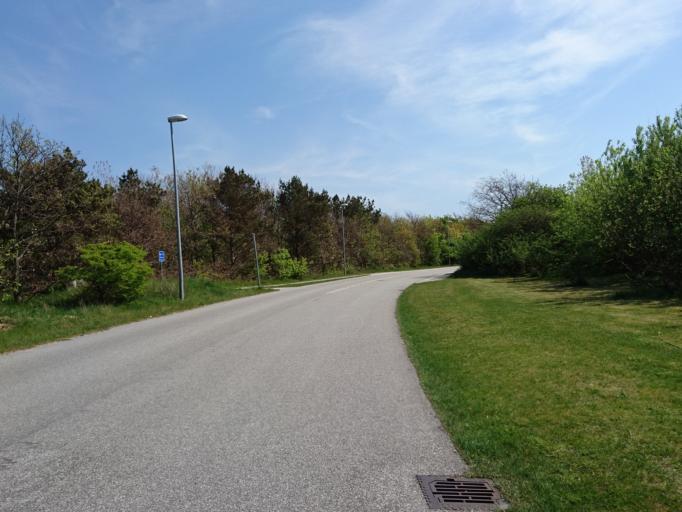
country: DK
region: North Denmark
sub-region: Frederikshavn Kommune
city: Skagen
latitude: 57.7346
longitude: 10.5962
